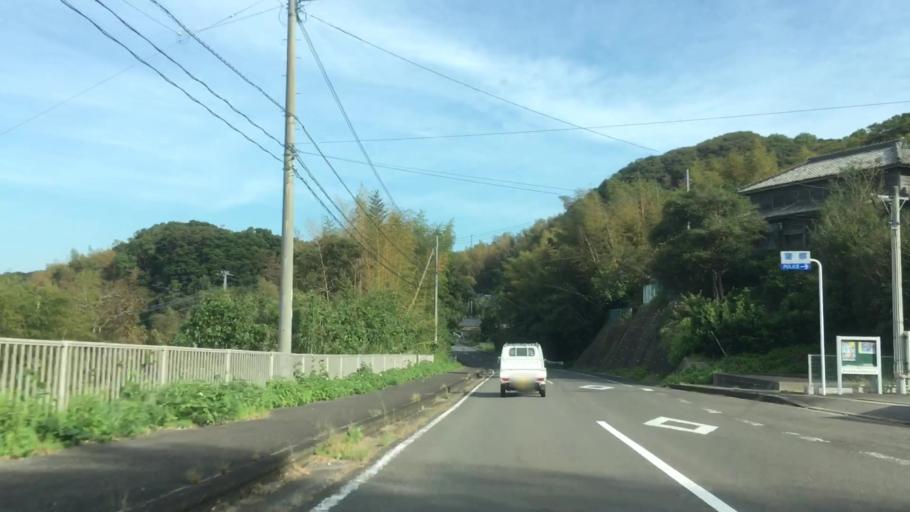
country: JP
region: Nagasaki
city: Sasebo
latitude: 33.0172
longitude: 129.6542
